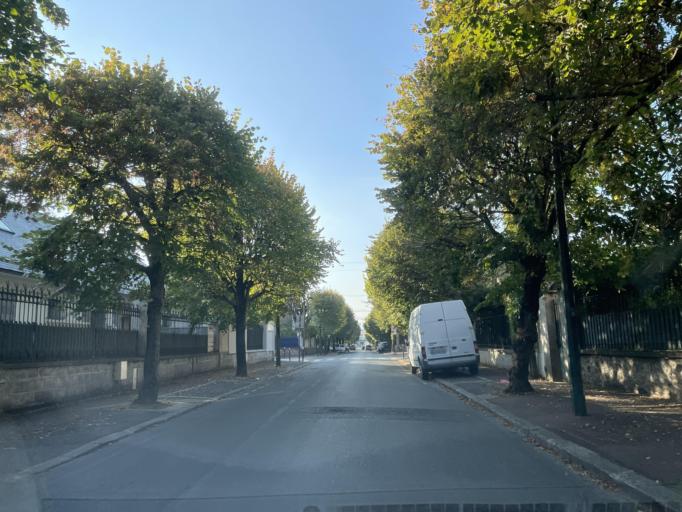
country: FR
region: Ile-de-France
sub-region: Departement du Val-de-Marne
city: Champigny-sur-Marne
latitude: 48.8067
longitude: 2.5133
